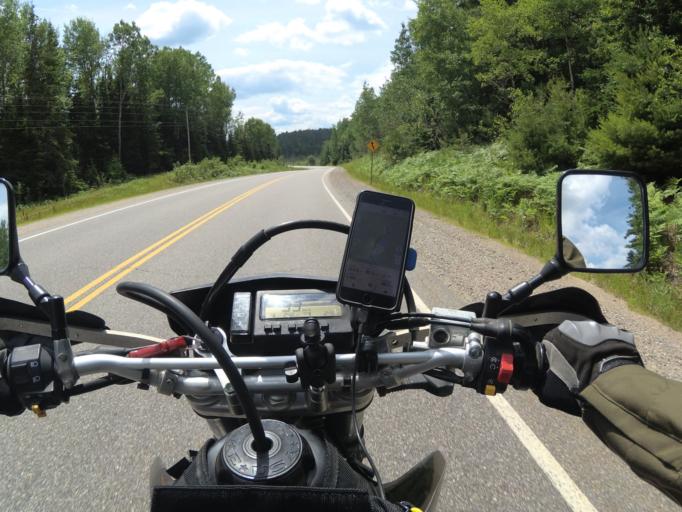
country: CA
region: Ontario
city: Bancroft
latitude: 45.0176
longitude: -77.2713
